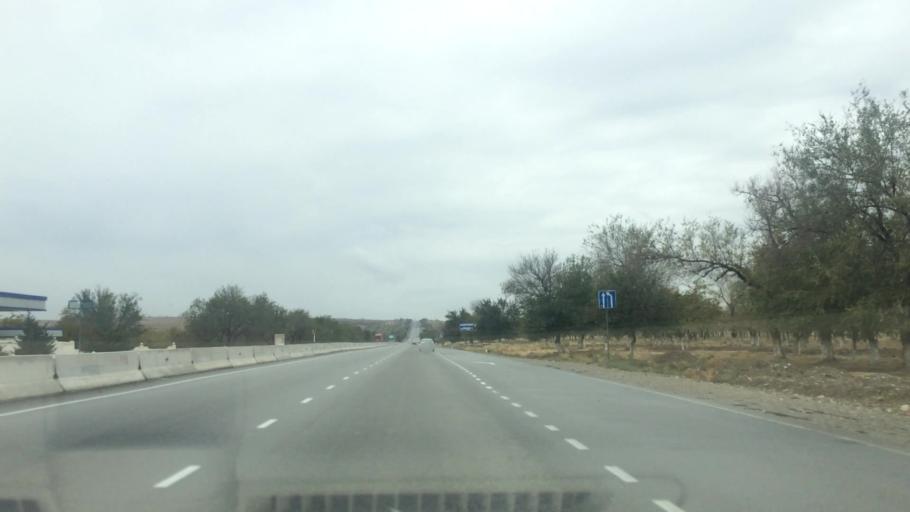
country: UZ
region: Samarqand
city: Bulung'ur
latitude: 39.8806
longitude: 67.4856
